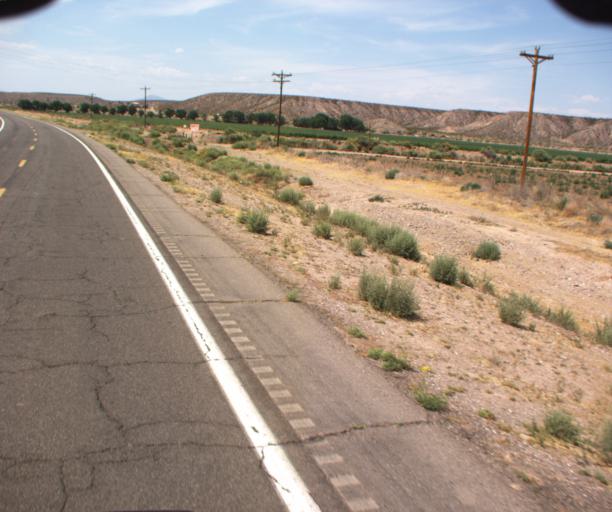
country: US
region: Arizona
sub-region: Greenlee County
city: Clifton
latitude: 32.8553
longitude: -109.1823
